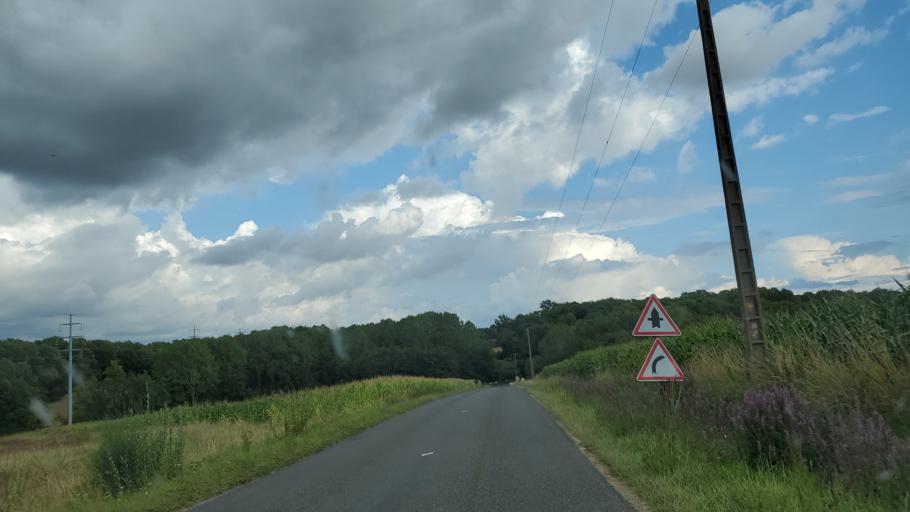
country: FR
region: Ile-de-France
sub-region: Departement de Seine-et-Marne
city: Chailly-en-Brie
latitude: 48.7802
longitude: 3.1672
